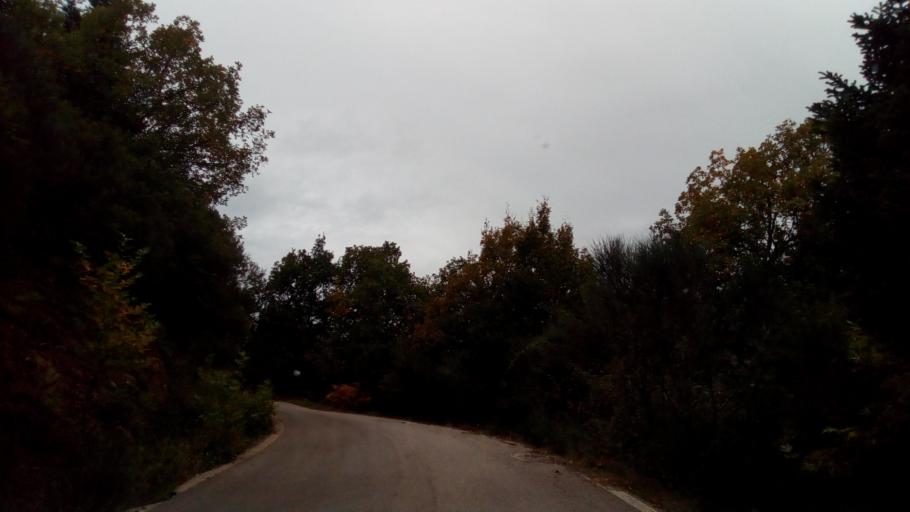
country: GR
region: West Greece
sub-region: Nomos Aitolias kai Akarnanias
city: Thermo
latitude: 38.5882
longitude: 21.8469
